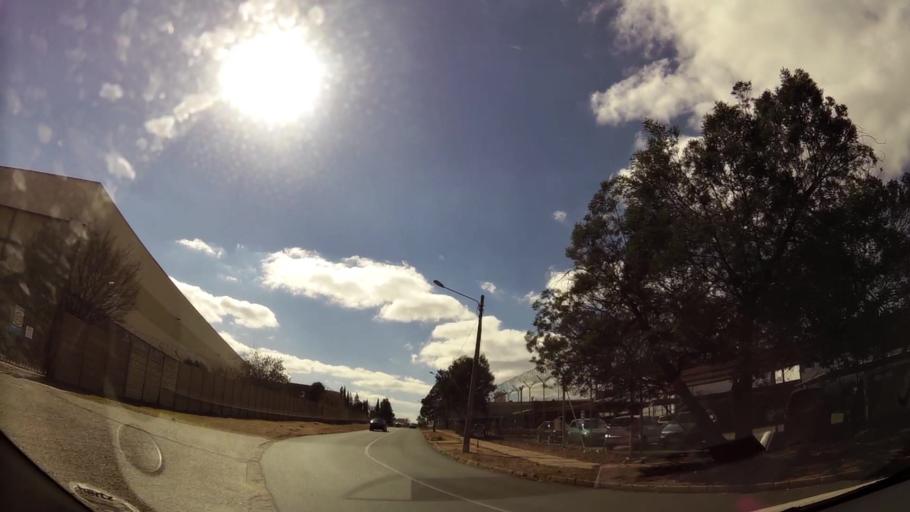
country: ZA
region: Gauteng
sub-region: West Rand District Municipality
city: Krugersdorp
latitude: -26.1151
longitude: 27.8092
